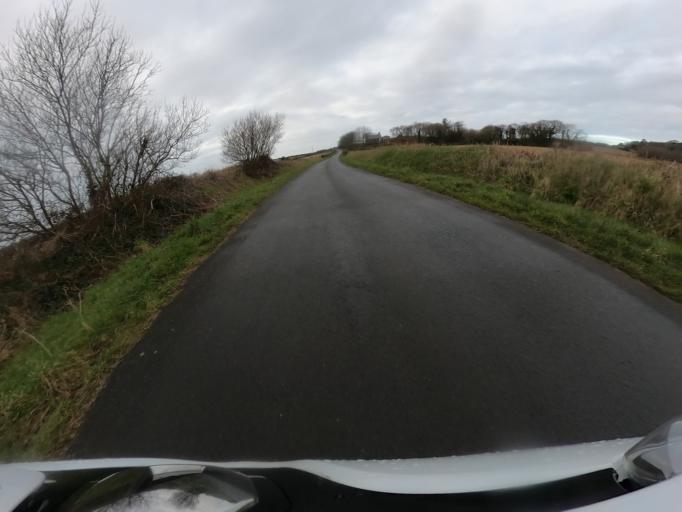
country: IM
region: Ramsey
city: Ramsey
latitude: 54.3469
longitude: -4.5199
